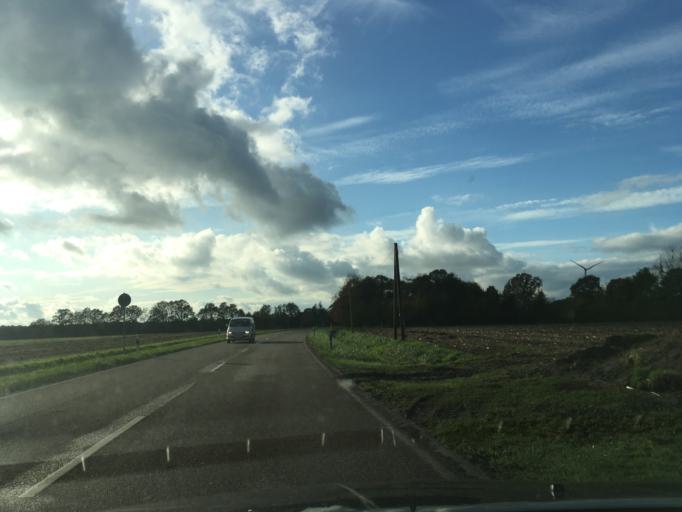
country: DE
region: North Rhine-Westphalia
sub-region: Regierungsbezirk Munster
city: Vreden
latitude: 52.0947
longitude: 6.8420
